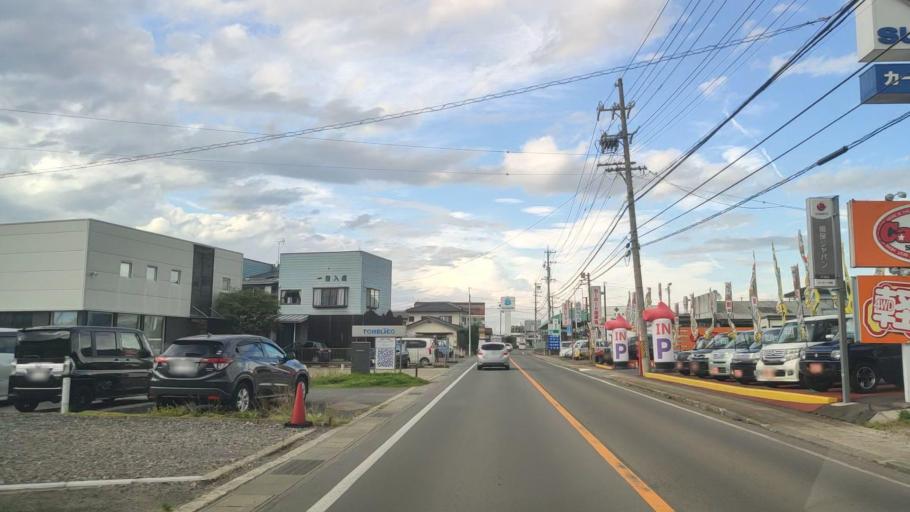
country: JP
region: Nagano
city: Suzaka
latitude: 36.6697
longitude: 138.3158
